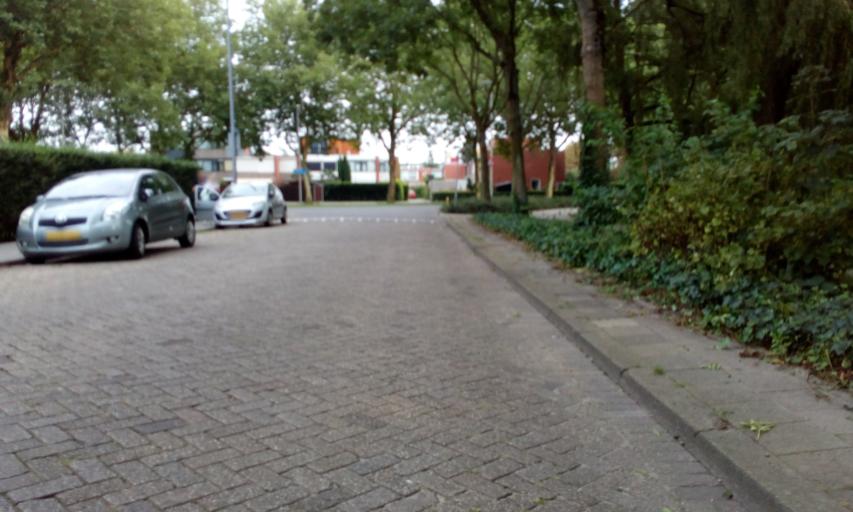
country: NL
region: South Holland
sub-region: Gemeente Rotterdam
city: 's-Gravenland
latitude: 51.9553
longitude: 4.5361
